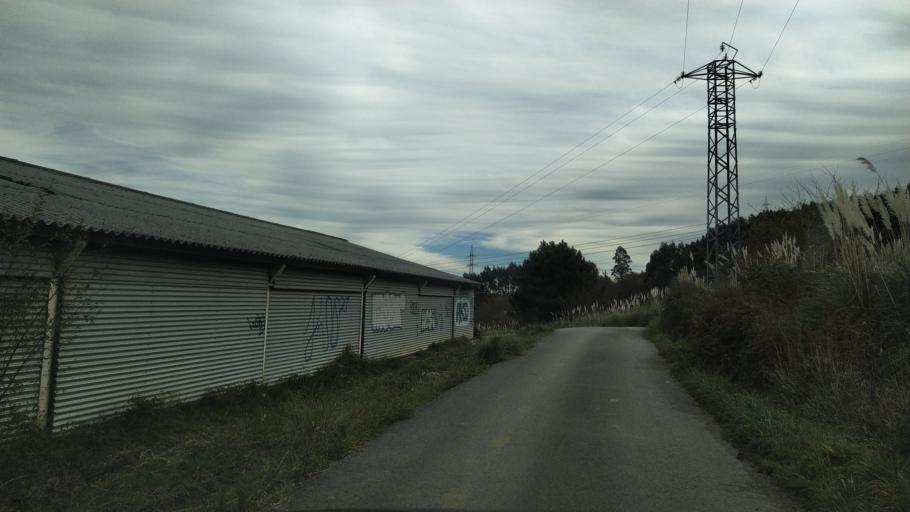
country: ES
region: Cantabria
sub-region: Provincia de Cantabria
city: Reocin
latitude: 43.3540
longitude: -4.0842
